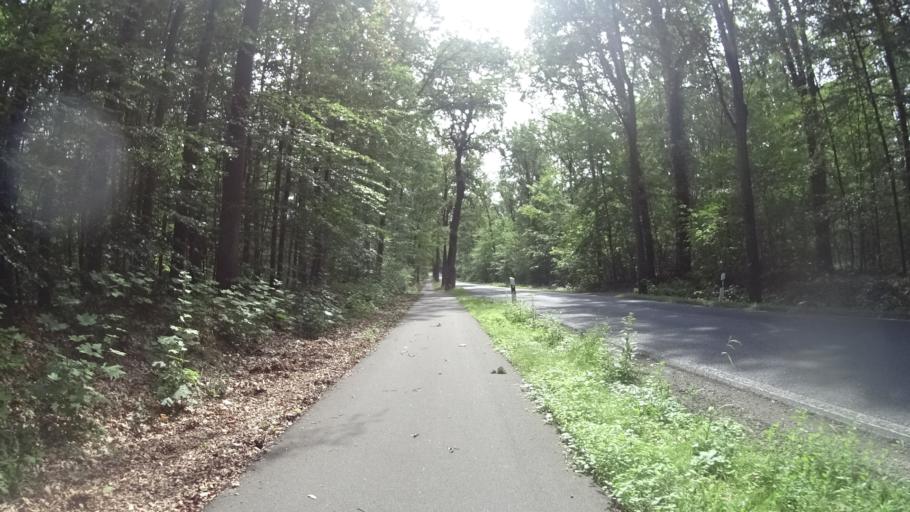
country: DE
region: Brandenburg
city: Gross Kreutz
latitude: 52.3118
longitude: 12.7512
